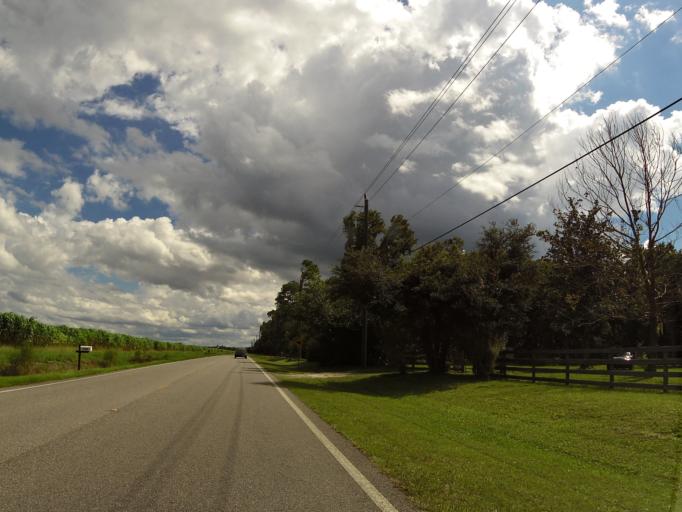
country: US
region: Florida
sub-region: Saint Johns County
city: Saint Augustine South
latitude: 29.8117
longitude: -81.4846
